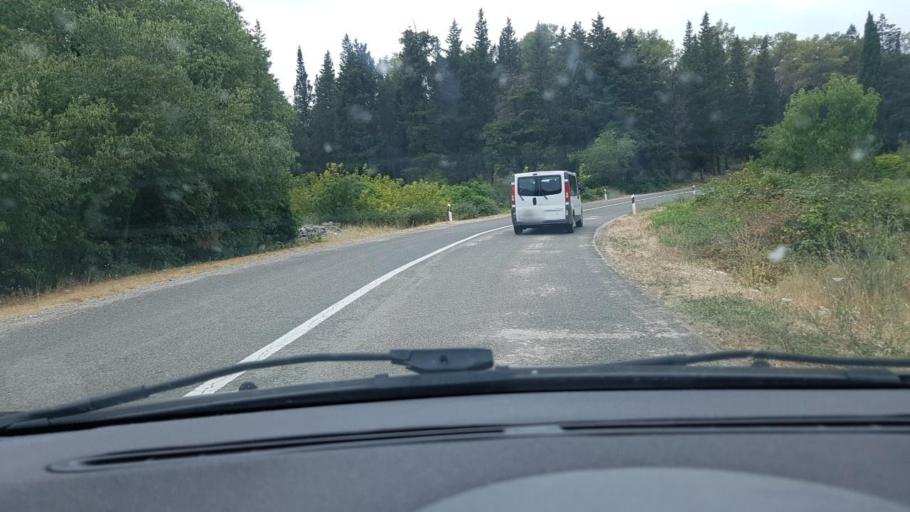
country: HR
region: Dubrovacko-Neretvanska
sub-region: Grad Korcula
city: Zrnovo
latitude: 42.9478
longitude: 17.0354
